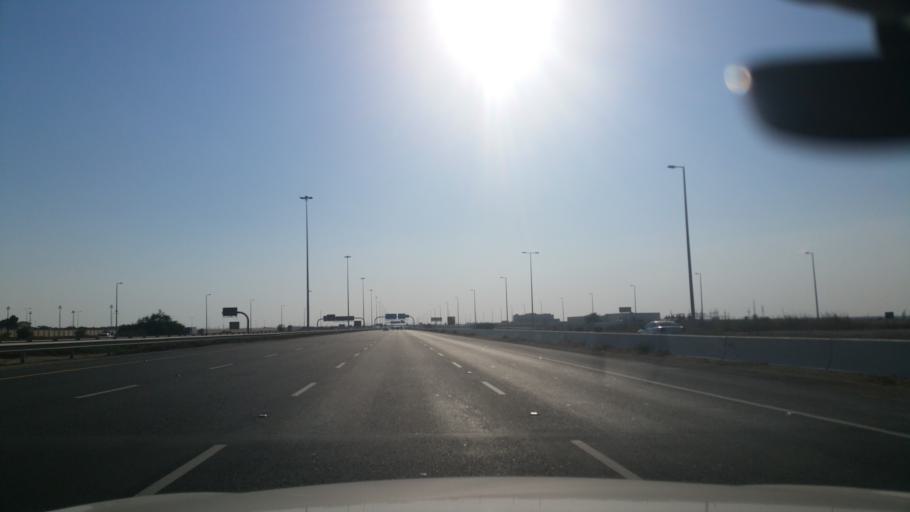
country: QA
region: Baladiyat ar Rayyan
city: Ar Rayyan
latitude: 25.2098
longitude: 51.4042
